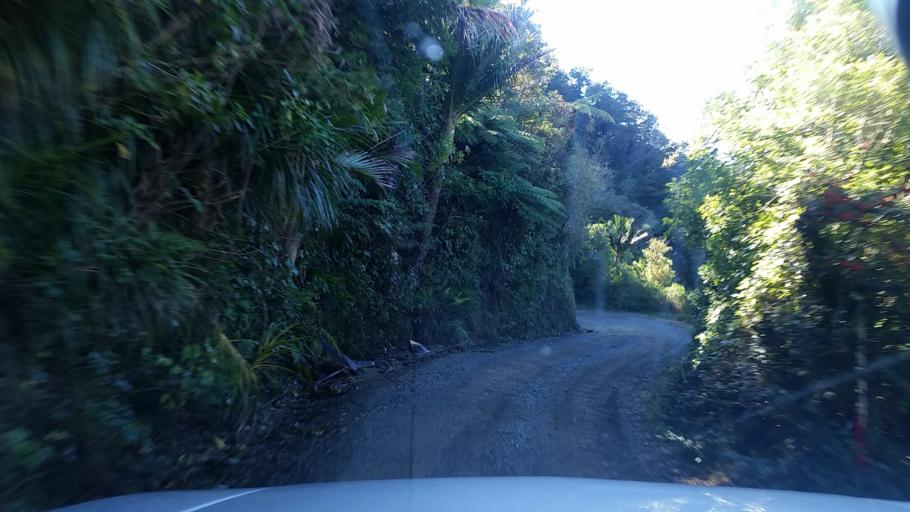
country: NZ
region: Marlborough
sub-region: Marlborough District
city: Picton
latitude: -41.1048
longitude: 173.6552
